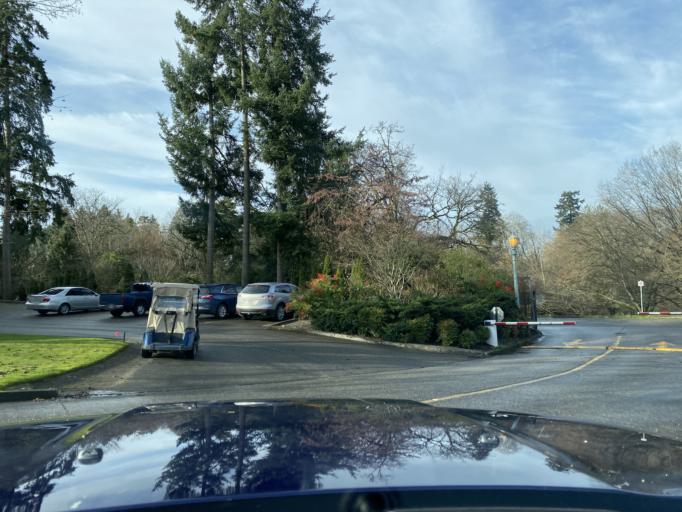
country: US
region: Washington
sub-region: King County
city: Seattle
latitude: 47.6409
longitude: -122.2926
